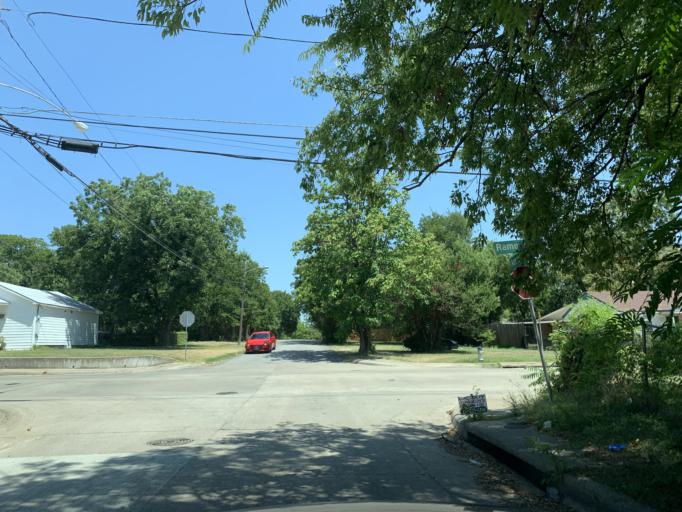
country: US
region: Texas
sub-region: Dallas County
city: Hutchins
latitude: 32.6882
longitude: -96.7992
